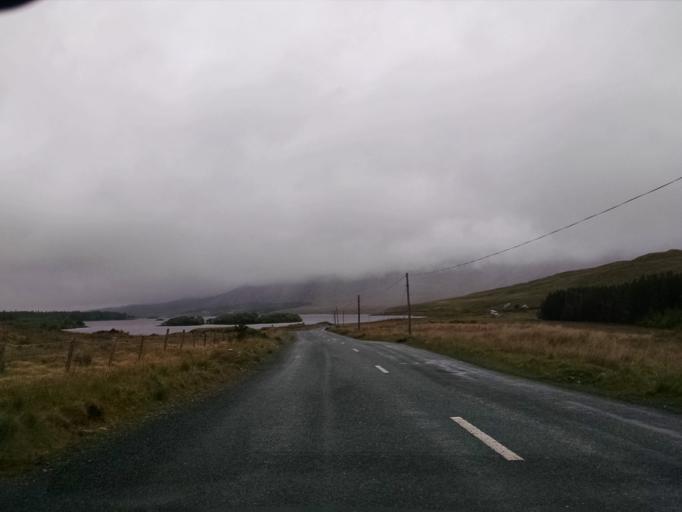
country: IE
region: Connaught
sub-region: County Galway
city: Clifden
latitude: 53.4901
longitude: -9.7388
